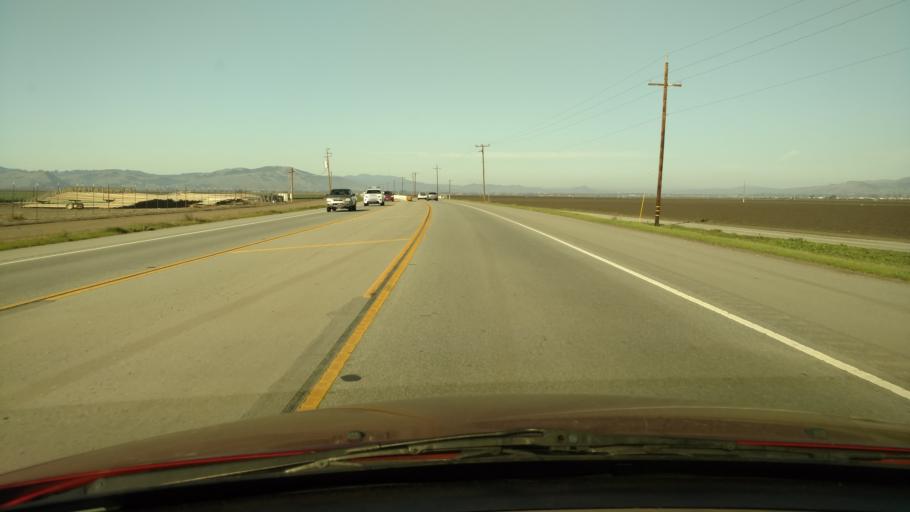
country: US
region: California
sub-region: San Benito County
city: Hollister
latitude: 36.9193
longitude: -121.4509
